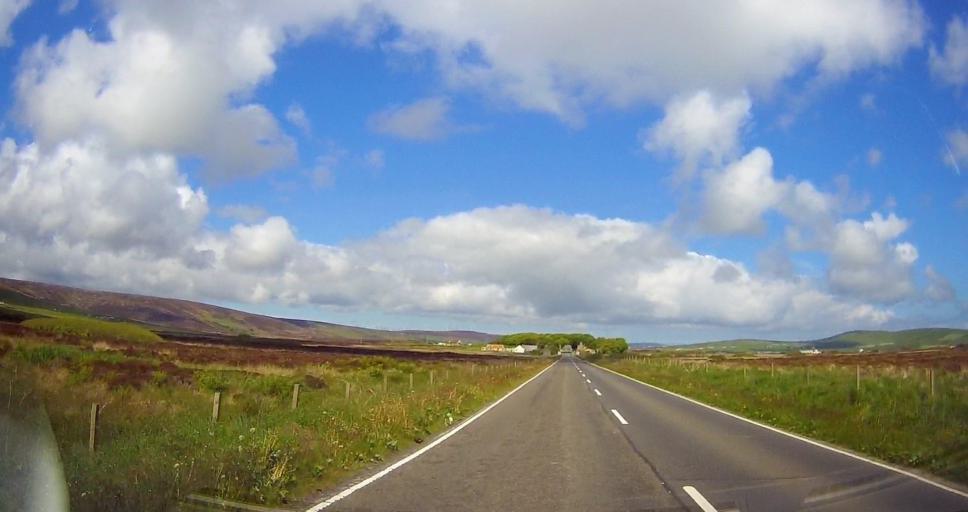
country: GB
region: Scotland
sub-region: Orkney Islands
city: Orkney
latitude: 59.0423
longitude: -3.0858
